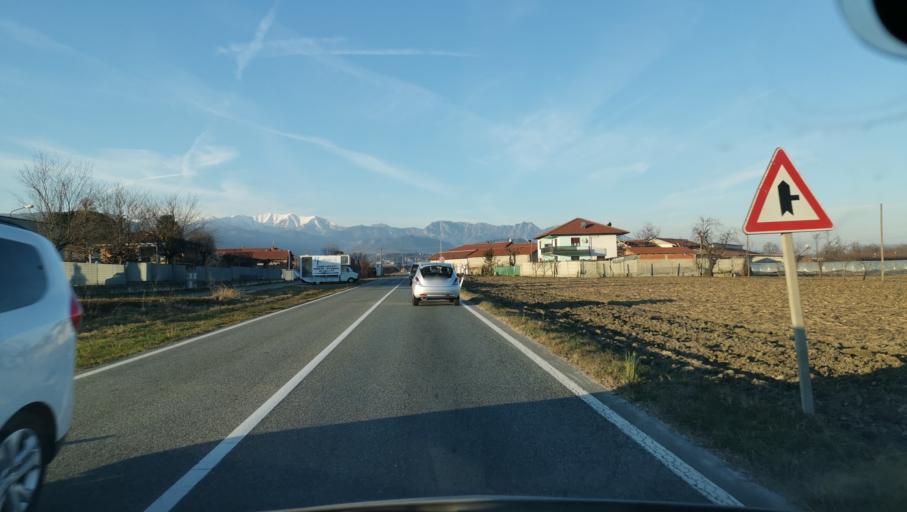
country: IT
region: Piedmont
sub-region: Provincia di Torino
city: Osasco
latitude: 44.8587
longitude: 7.3355
